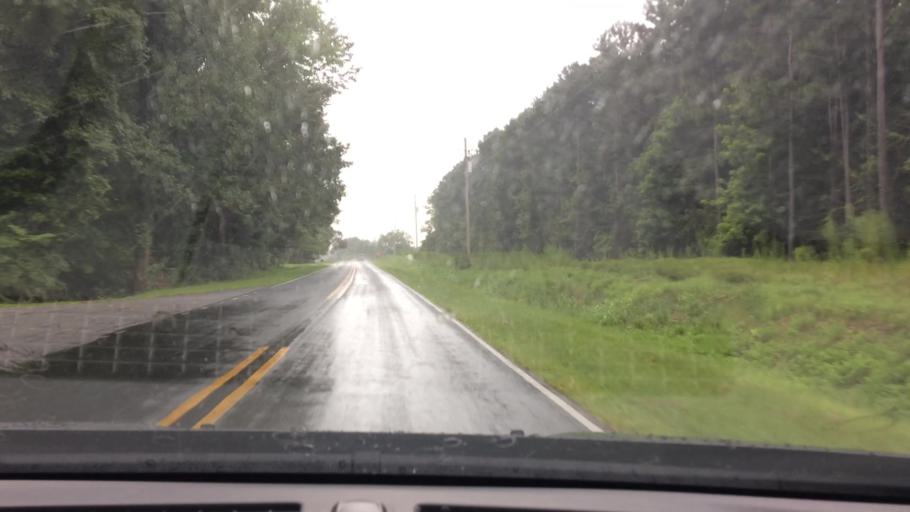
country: US
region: North Carolina
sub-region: Pitt County
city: Summerfield
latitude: 35.6115
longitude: -77.4146
